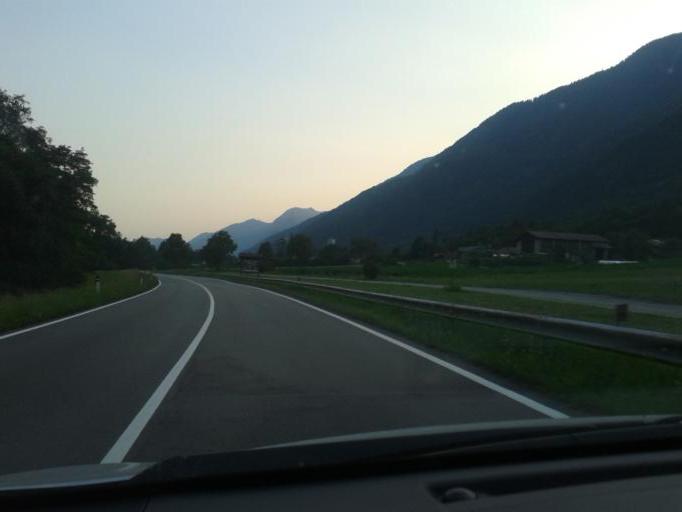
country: IT
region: Trentino-Alto Adige
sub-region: Provincia di Trento
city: Storo
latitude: 45.8647
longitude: 10.5773
